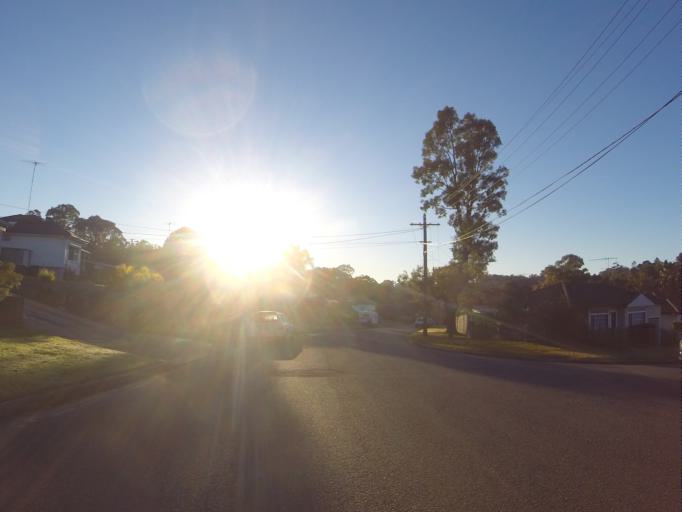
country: AU
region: New South Wales
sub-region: Sutherland Shire
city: Engadine
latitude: -34.0523
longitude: 151.0098
